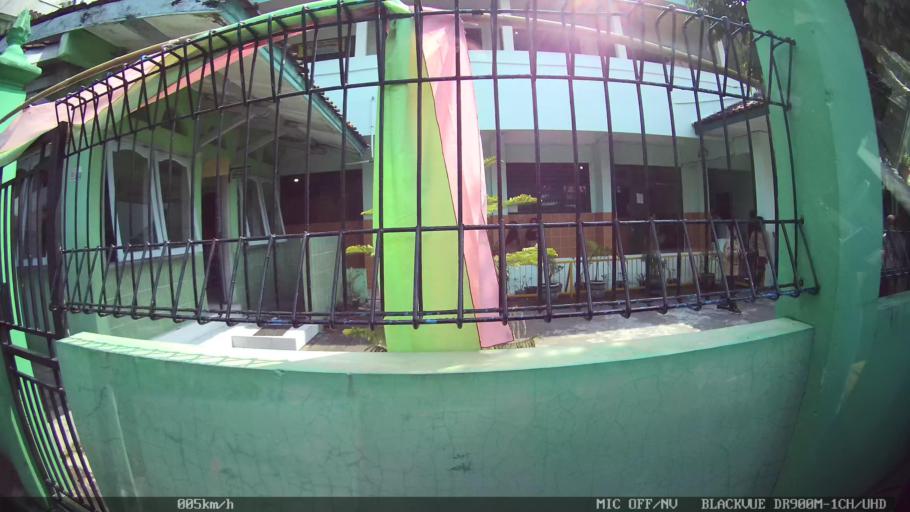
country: ID
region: Daerah Istimewa Yogyakarta
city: Yogyakarta
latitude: -7.8054
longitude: 110.3910
